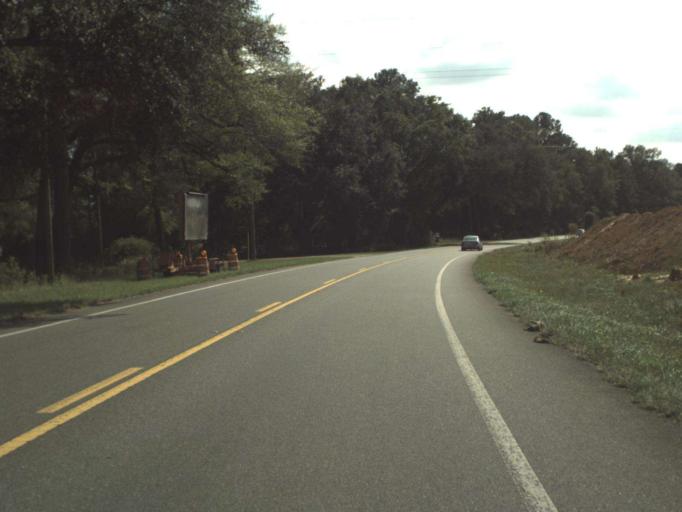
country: US
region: Florida
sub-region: Holmes County
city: Bonifay
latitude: 30.6503
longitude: -85.6984
